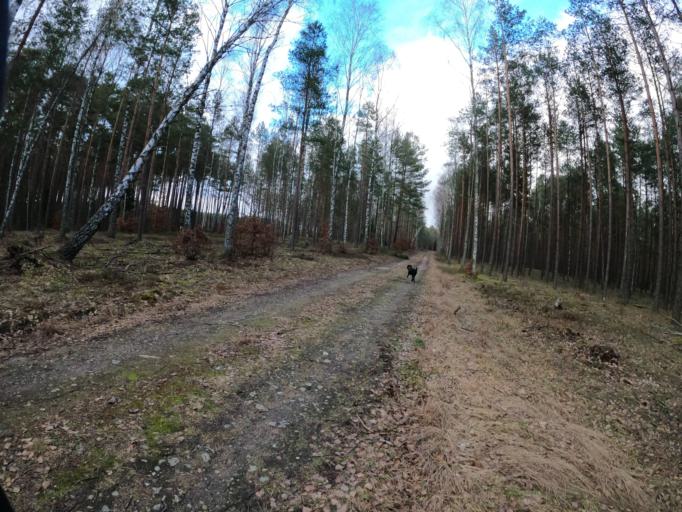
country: PL
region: Greater Poland Voivodeship
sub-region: Powiat zlotowski
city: Sypniewo
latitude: 53.4399
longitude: 16.5829
